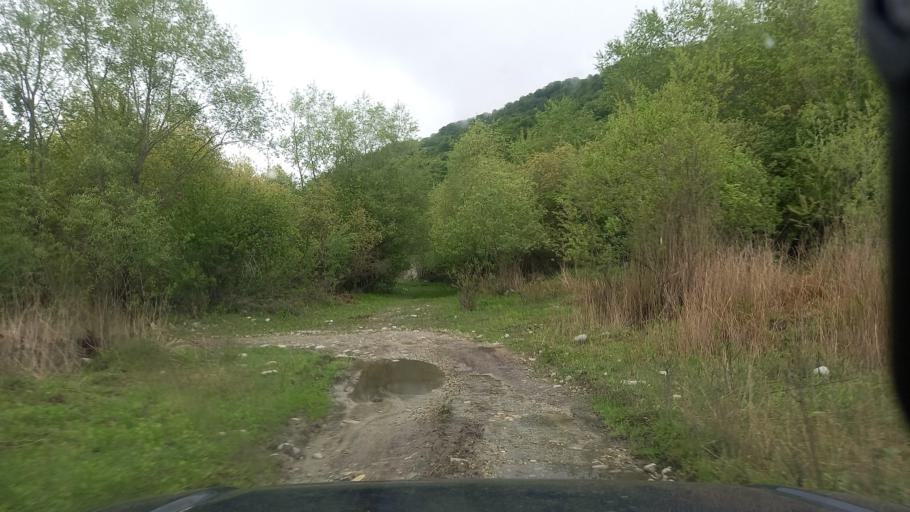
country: RU
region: Kabardino-Balkariya
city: Kashkhatau
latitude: 43.2966
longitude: 43.5900
